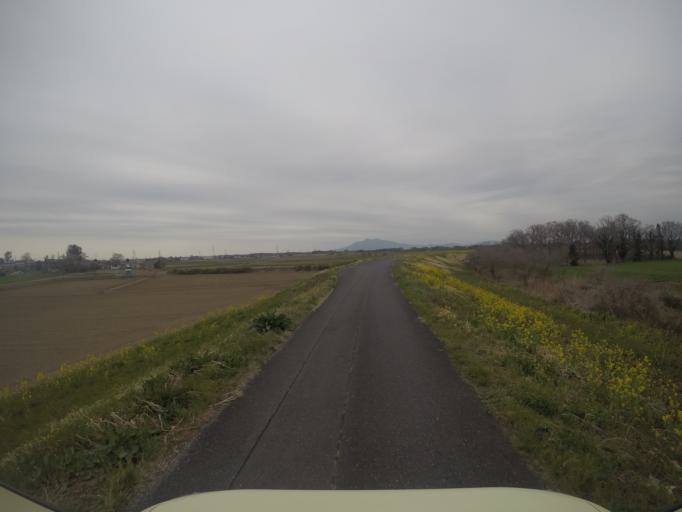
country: JP
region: Ibaraki
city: Ishige
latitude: 36.0915
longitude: 139.9973
